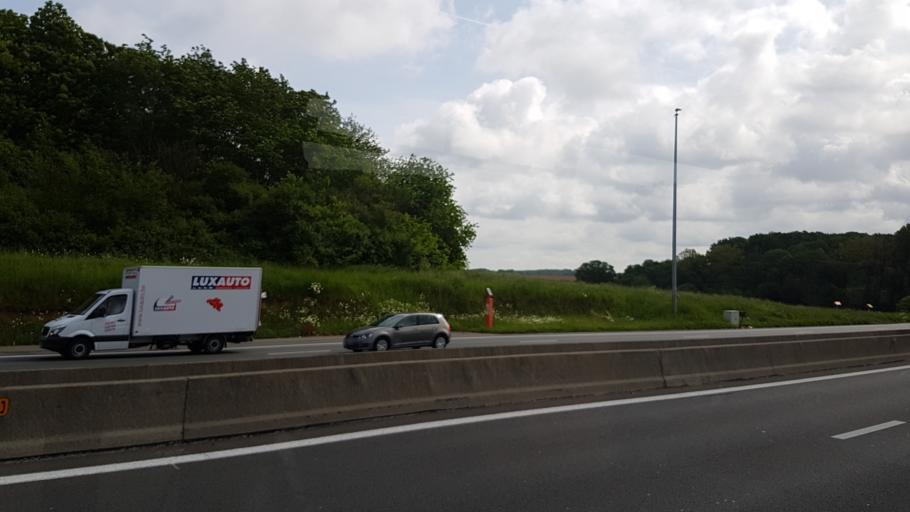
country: BE
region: Flanders
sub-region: Provincie Vlaams-Brabant
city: Bertem
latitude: 50.8653
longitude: 4.5841
